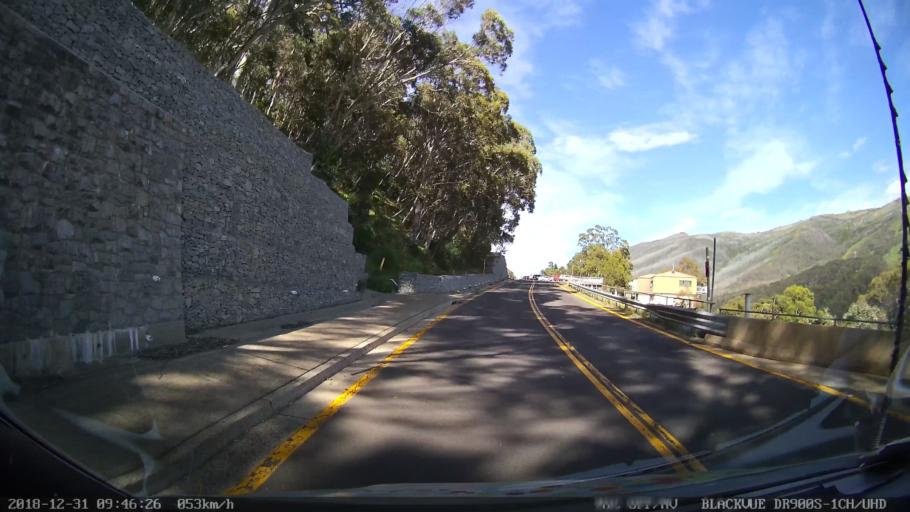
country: AU
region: New South Wales
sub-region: Snowy River
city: Jindabyne
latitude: -36.5038
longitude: 148.3094
